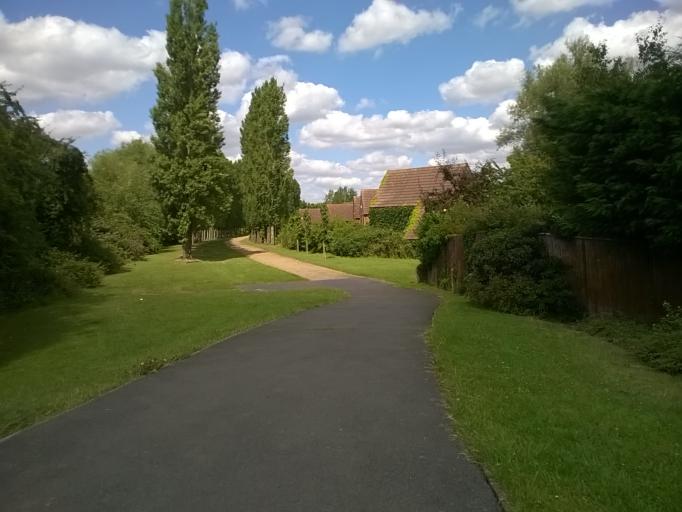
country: GB
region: England
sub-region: Milton Keynes
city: Milton Keynes
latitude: 52.0589
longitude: -0.7356
